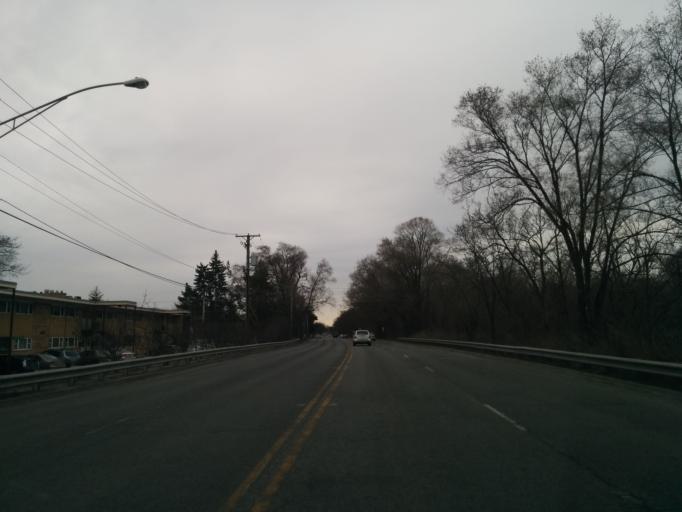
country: US
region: Illinois
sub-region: Cook County
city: Westchester
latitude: 41.8429
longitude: -87.8783
